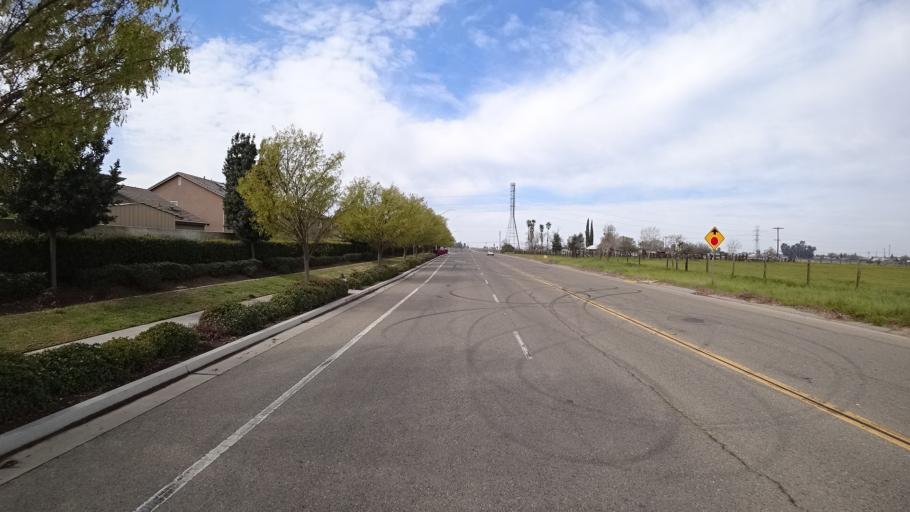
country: US
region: California
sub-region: Fresno County
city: West Park
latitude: 36.7862
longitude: -119.8962
